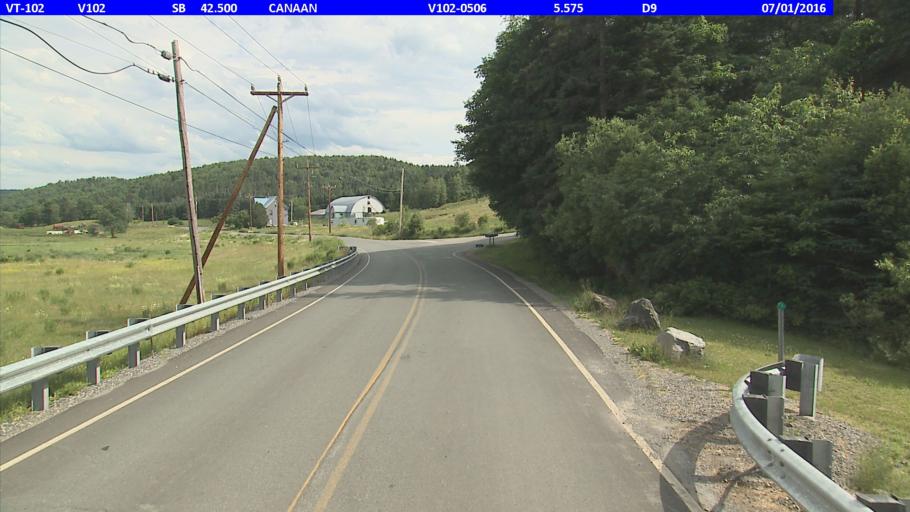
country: US
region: New Hampshire
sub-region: Coos County
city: Colebrook
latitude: 44.9793
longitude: -71.5419
